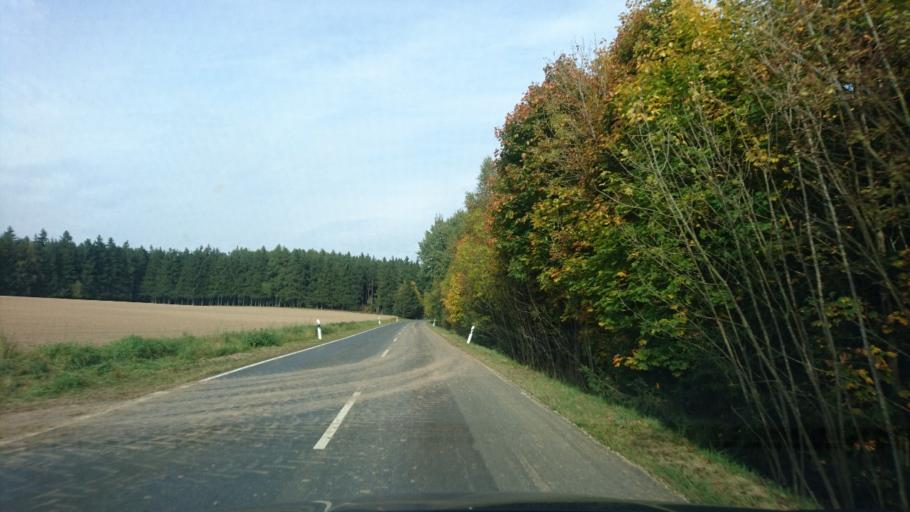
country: DE
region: Bavaria
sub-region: Upper Franconia
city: Naila
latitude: 50.3303
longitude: 11.7276
